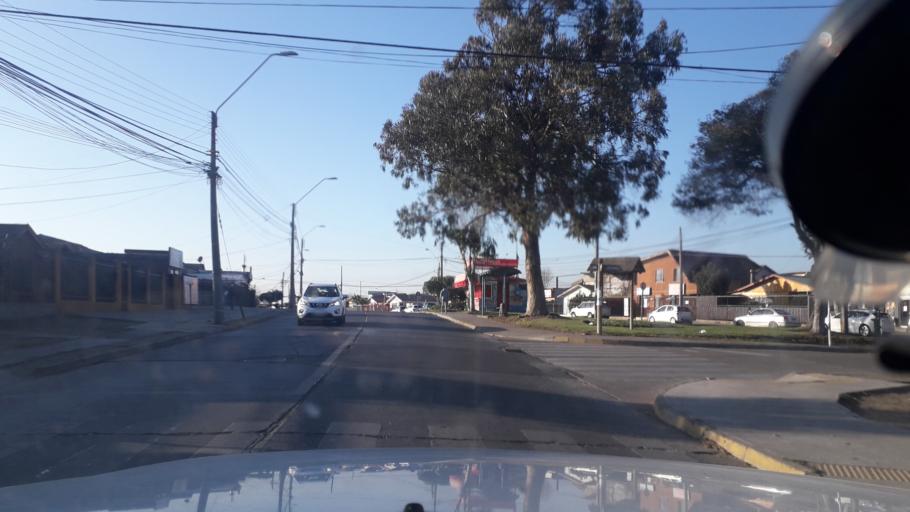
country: CL
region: Valparaiso
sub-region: Provincia de Valparaiso
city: Vina del Mar
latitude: -32.9276
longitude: -71.5170
